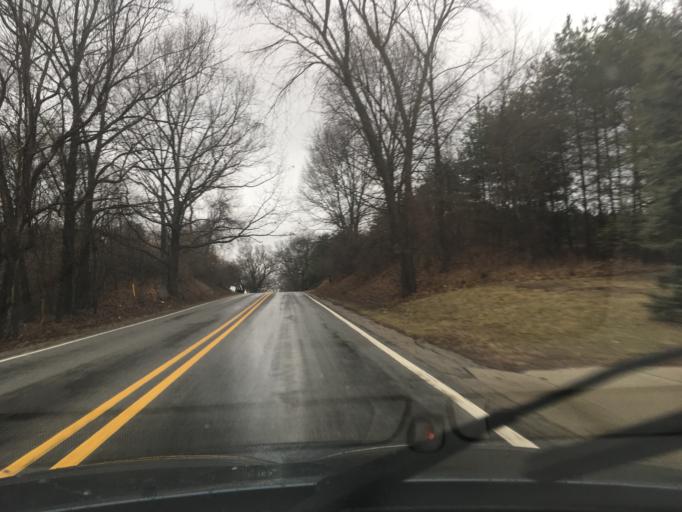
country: US
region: Michigan
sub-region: Washtenaw County
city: Chelsea
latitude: 42.3091
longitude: -84.0773
